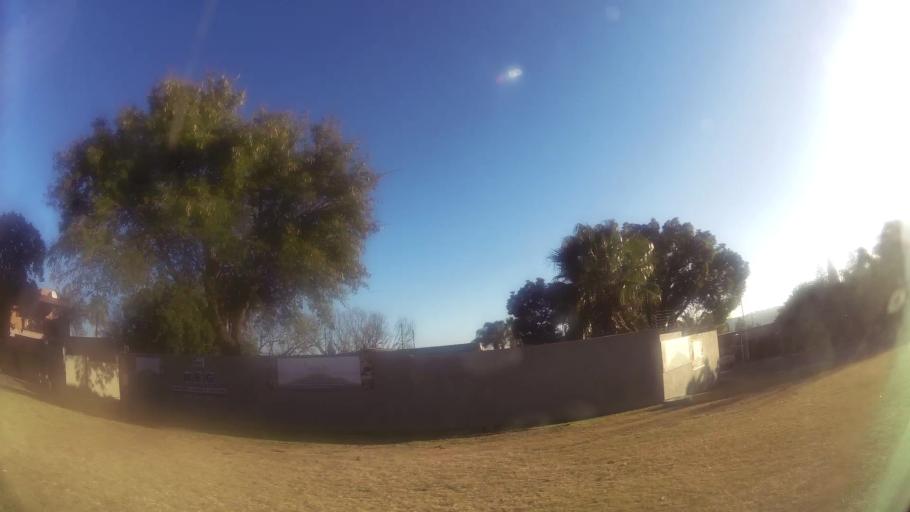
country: ZA
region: Gauteng
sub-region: City of Tshwane Metropolitan Municipality
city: Centurion
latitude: -25.8947
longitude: 28.1324
